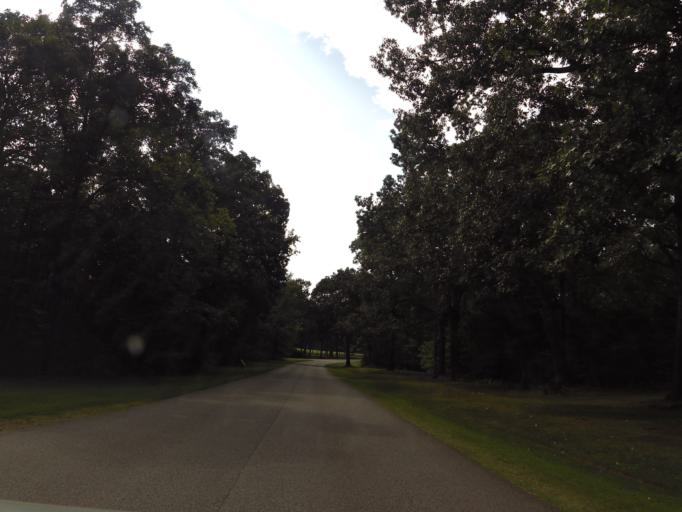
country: US
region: Tennessee
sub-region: Hardin County
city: Crump
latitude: 35.1508
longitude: -88.3266
